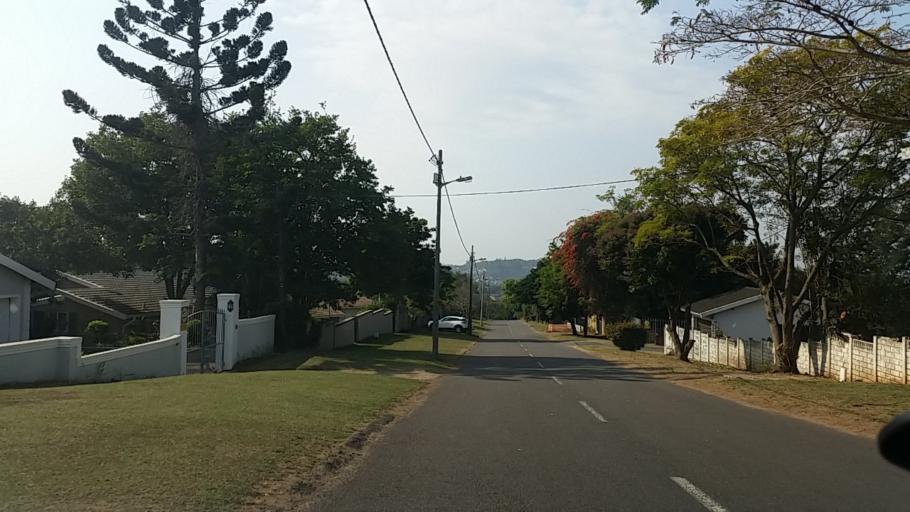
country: ZA
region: KwaZulu-Natal
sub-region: eThekwini Metropolitan Municipality
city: Berea
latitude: -29.8437
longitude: 30.9458
